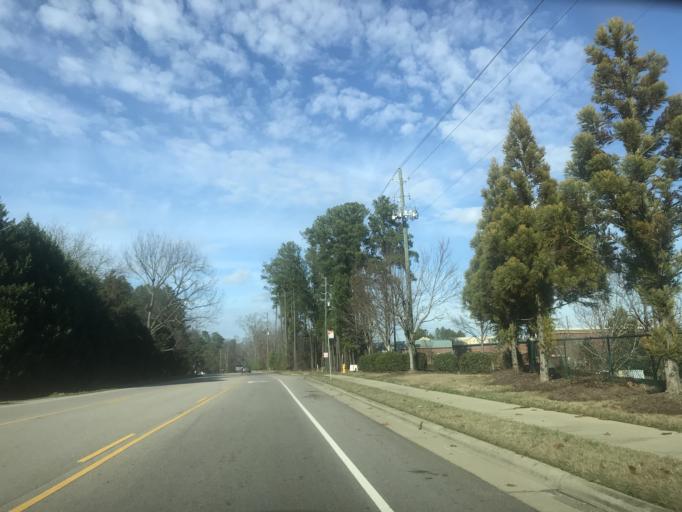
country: US
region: North Carolina
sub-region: Wake County
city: Garner
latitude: 35.7233
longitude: -78.5490
